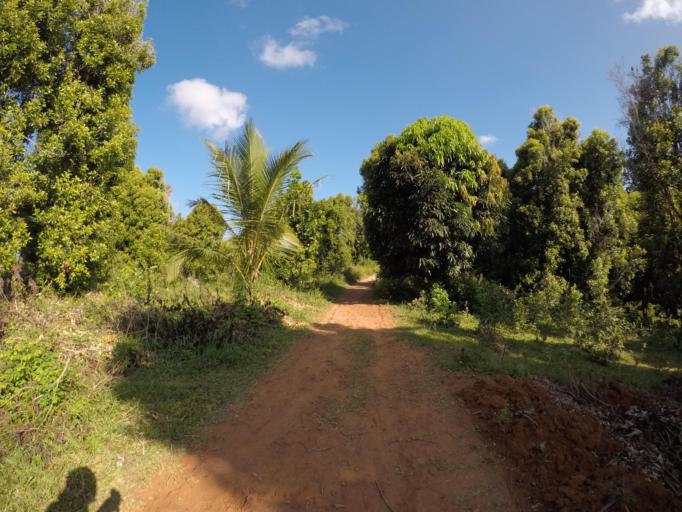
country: TZ
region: Pemba South
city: Mtambile
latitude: -5.3873
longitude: 39.7274
